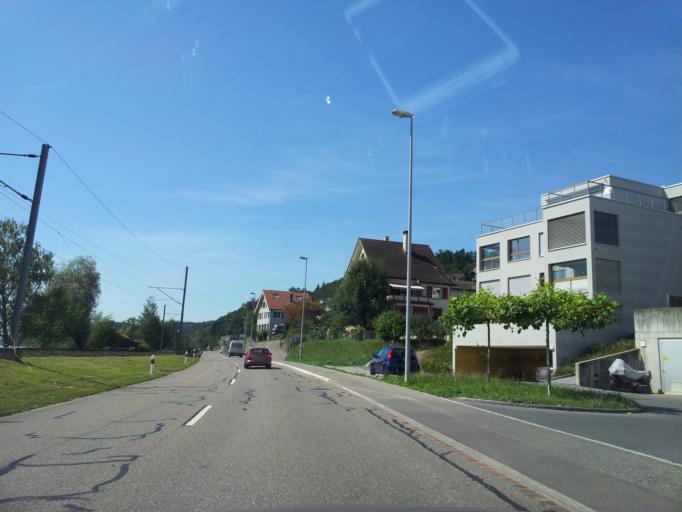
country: CH
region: Saint Gallen
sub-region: Wahlkreis See-Gaster
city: Schmerikon
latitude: 47.2256
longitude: 8.9371
